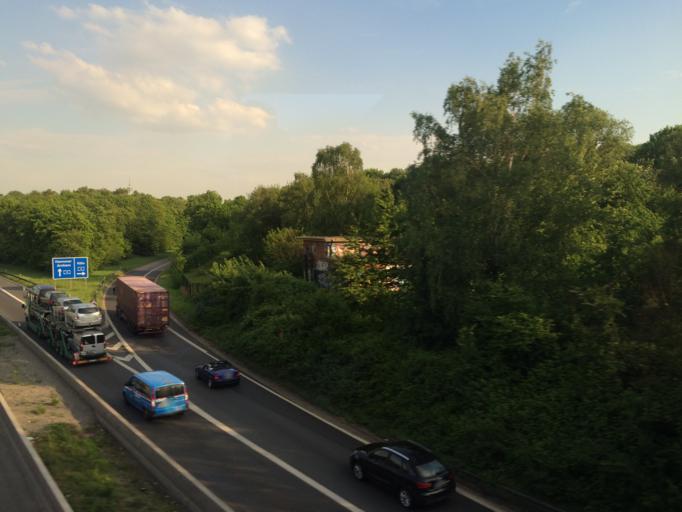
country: DE
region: North Rhine-Westphalia
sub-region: Regierungsbezirk Dusseldorf
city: Duisburg
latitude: 51.4445
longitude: 6.8013
